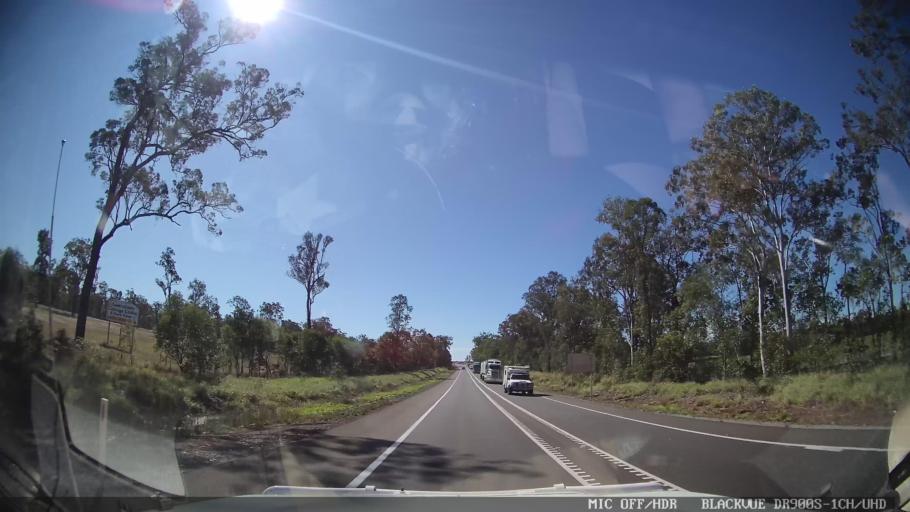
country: AU
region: Queensland
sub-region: Fraser Coast
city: Maryborough
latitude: -25.6505
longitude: 152.6332
